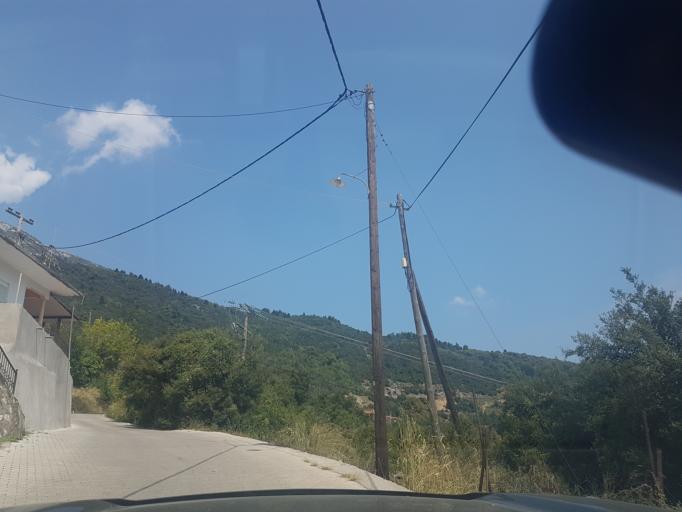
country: GR
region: Central Greece
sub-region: Nomos Evvoias
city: Yimnon
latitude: 38.6191
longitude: 23.8882
